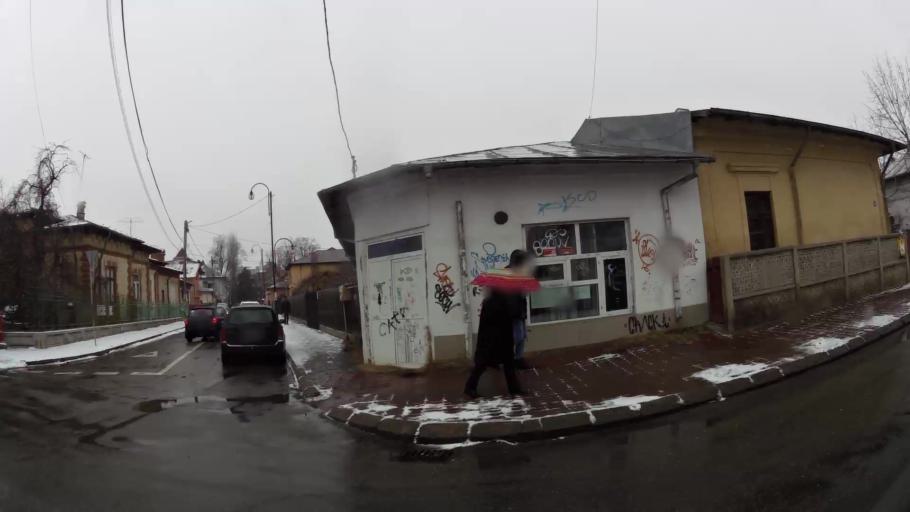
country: RO
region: Dambovita
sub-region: Municipiul Targoviste
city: Targoviste
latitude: 44.9277
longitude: 25.4526
